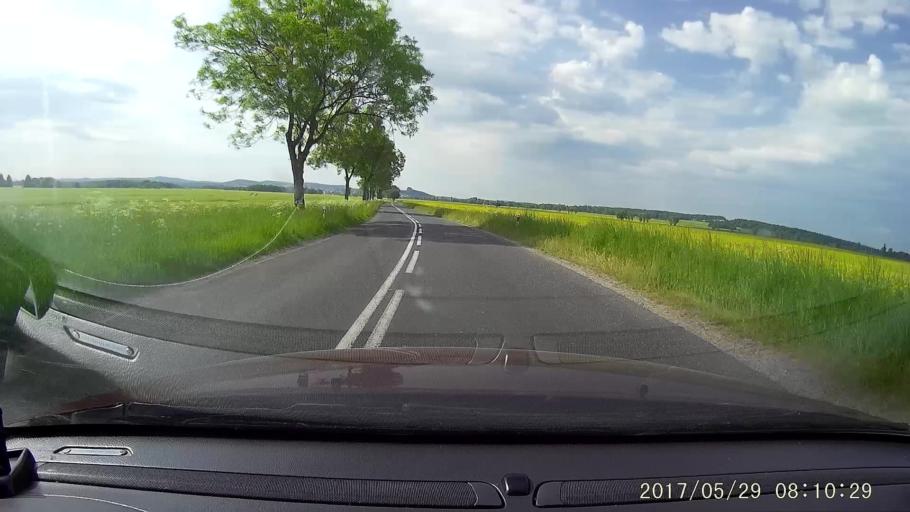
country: PL
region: Lower Silesian Voivodeship
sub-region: Powiat zlotoryjski
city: Zlotoryja
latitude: 51.1537
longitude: 15.9002
